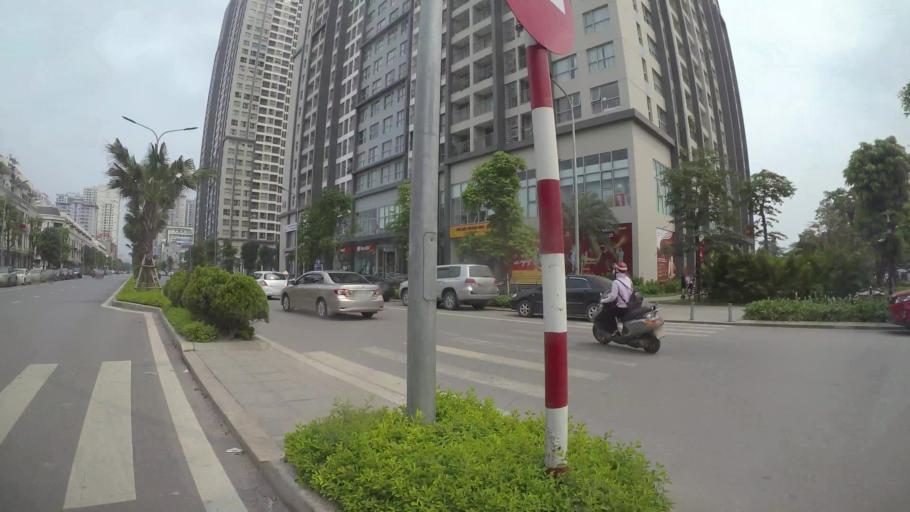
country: VN
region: Ha Noi
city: Cau Dien
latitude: 21.0364
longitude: 105.7599
